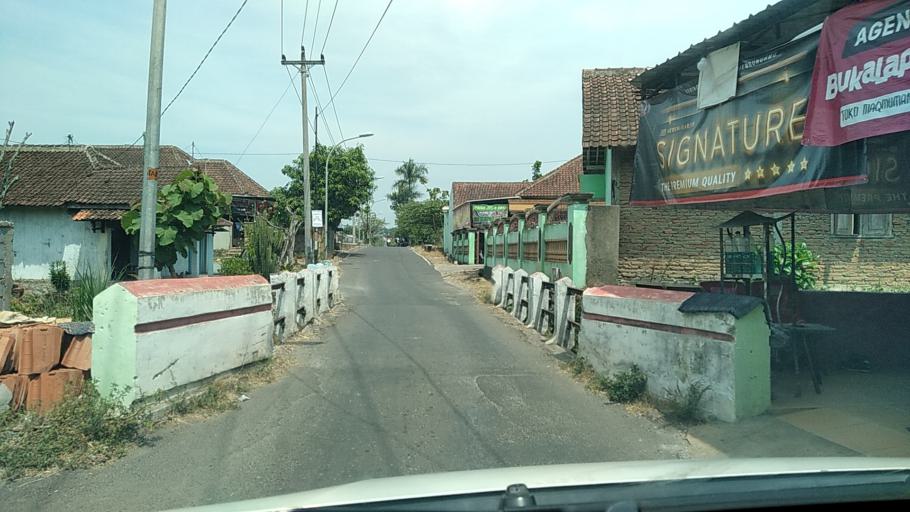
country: ID
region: Central Java
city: Ungaran
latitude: -7.0775
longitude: 110.3196
